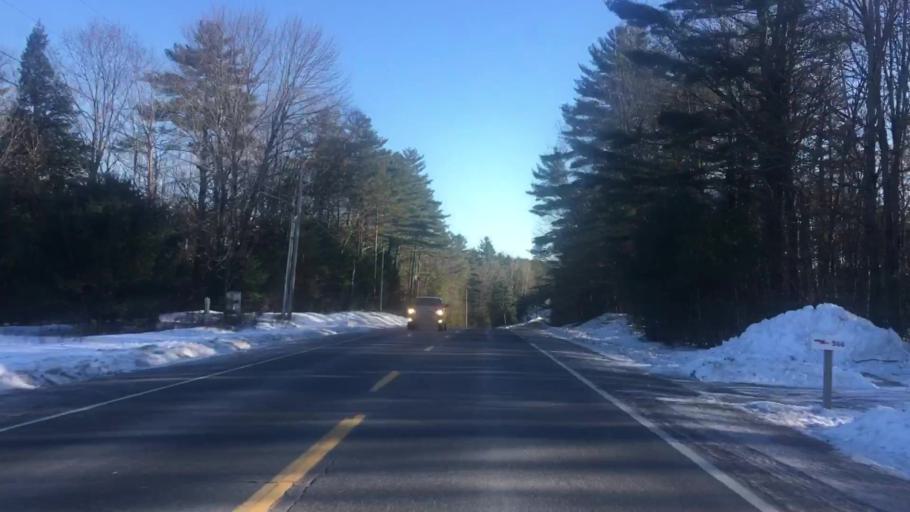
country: US
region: Maine
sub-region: Somerset County
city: Norridgewock
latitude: 44.7463
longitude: -69.8327
